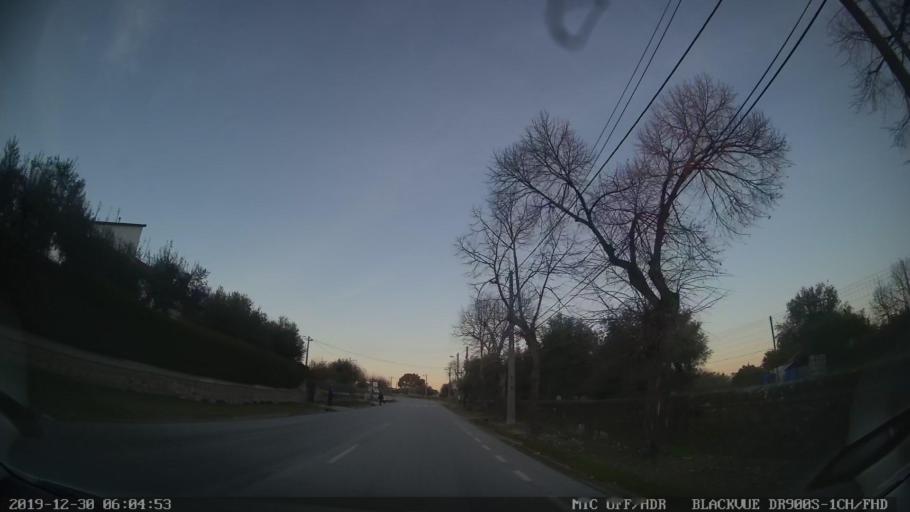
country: PT
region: Castelo Branco
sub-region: Penamacor
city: Penamacor
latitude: 40.0869
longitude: -7.2361
